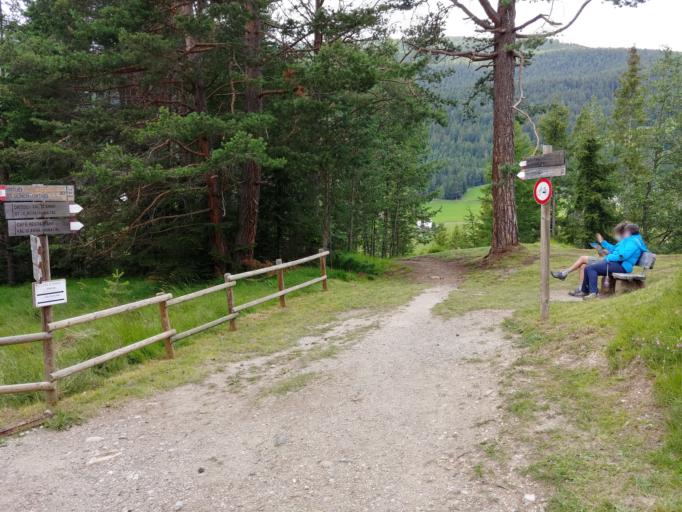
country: IT
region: Trentino-Alto Adige
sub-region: Bolzano
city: Ortisei
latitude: 46.5766
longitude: 11.6859
